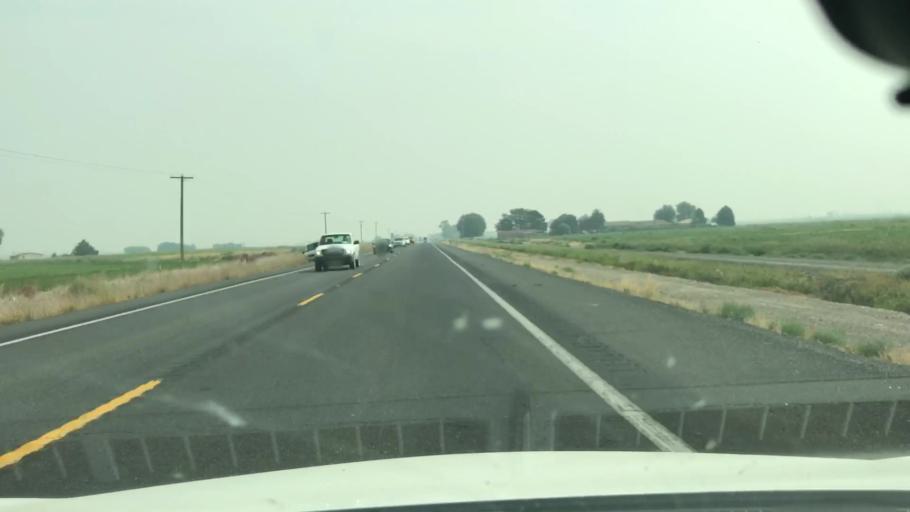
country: US
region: Washington
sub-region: Grant County
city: Quincy
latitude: 47.2343
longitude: -119.7834
